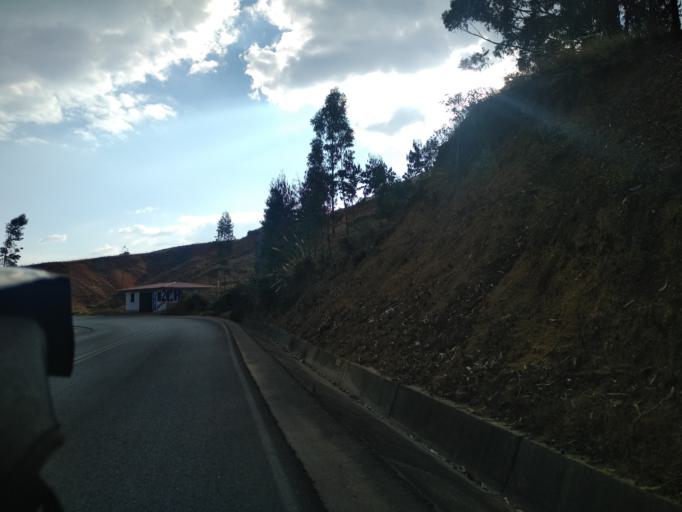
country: PE
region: Cajamarca
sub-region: Provincia de Cajamarca
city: Llacanora
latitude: -7.1525
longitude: -78.4138
